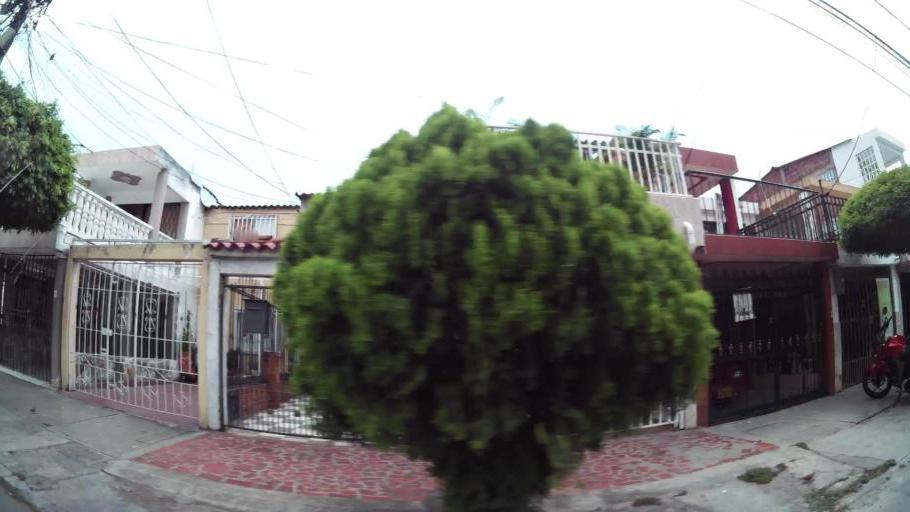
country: CO
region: Valle del Cauca
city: Cali
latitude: 3.4749
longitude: -76.5016
